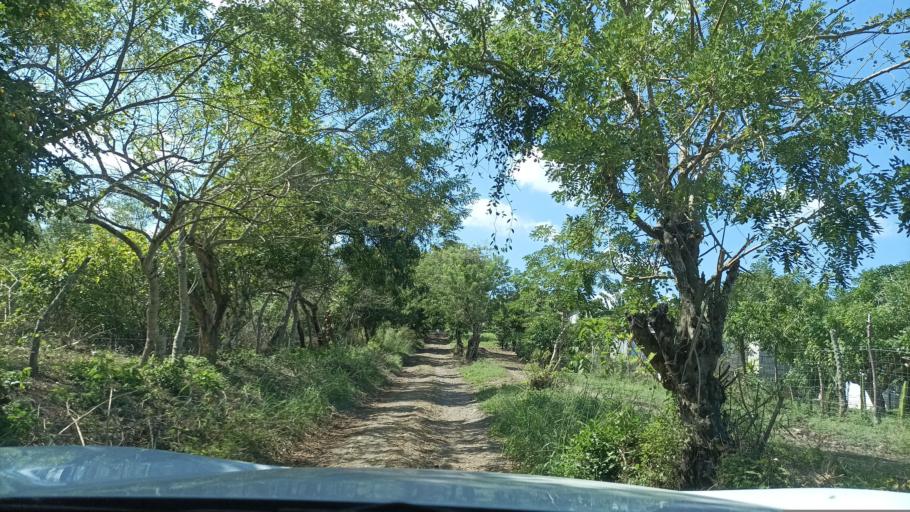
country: MX
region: Veracruz
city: Manlio Fabio Altamirano
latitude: 19.0882
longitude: -96.3408
